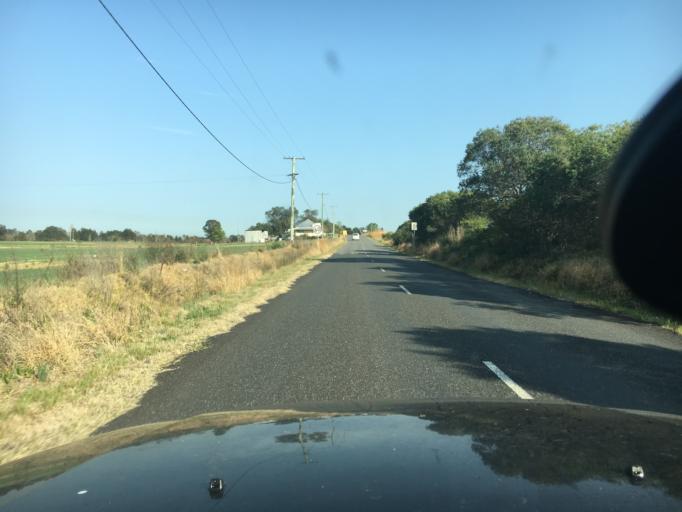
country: AU
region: New South Wales
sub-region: Cessnock
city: Branxton
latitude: -32.6043
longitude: 151.3426
